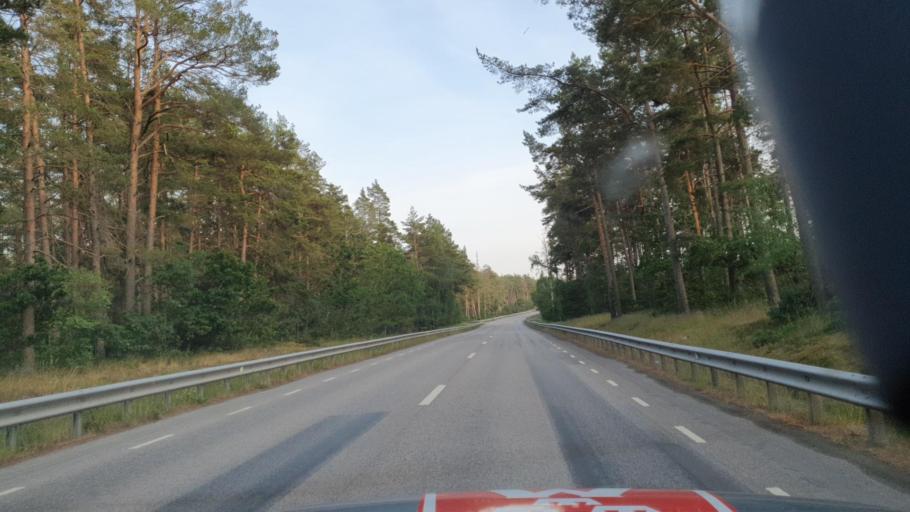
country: SE
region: Kalmar
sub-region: Kalmar Kommun
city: Ljungbyholm
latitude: 56.5896
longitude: 16.1684
